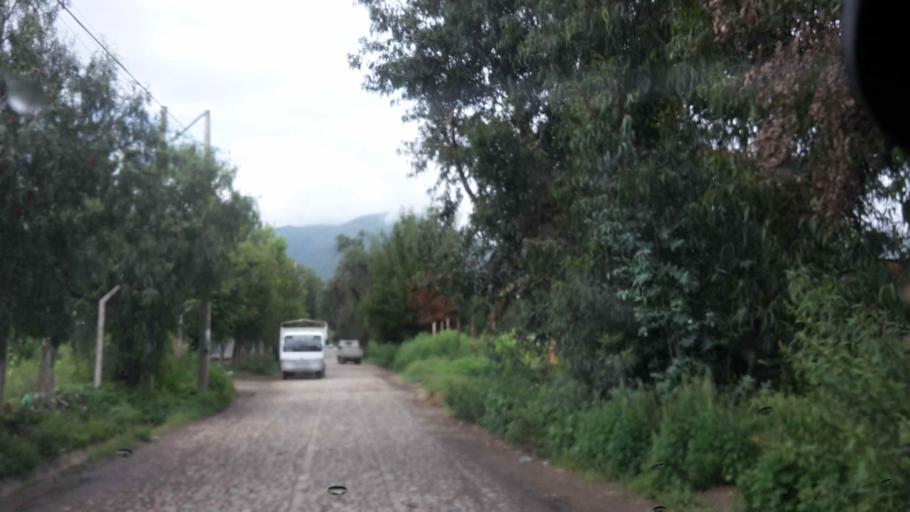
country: BO
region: Cochabamba
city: Cochabamba
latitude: -17.3654
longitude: -66.2138
